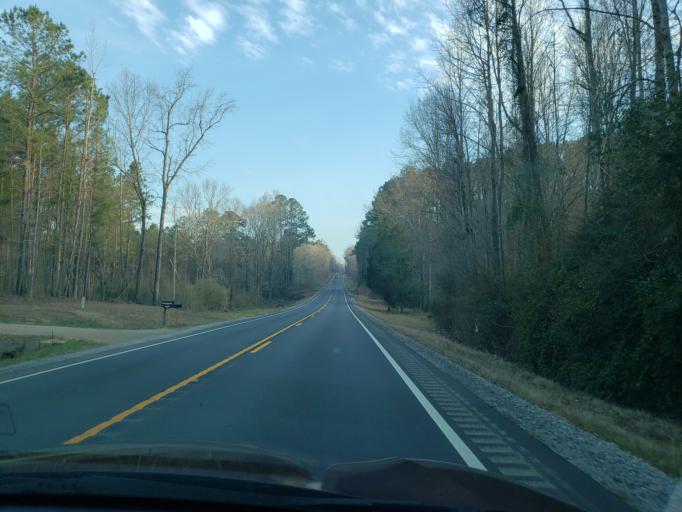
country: US
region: Alabama
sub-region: Hale County
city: Greensboro
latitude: 32.8169
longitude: -87.5984
